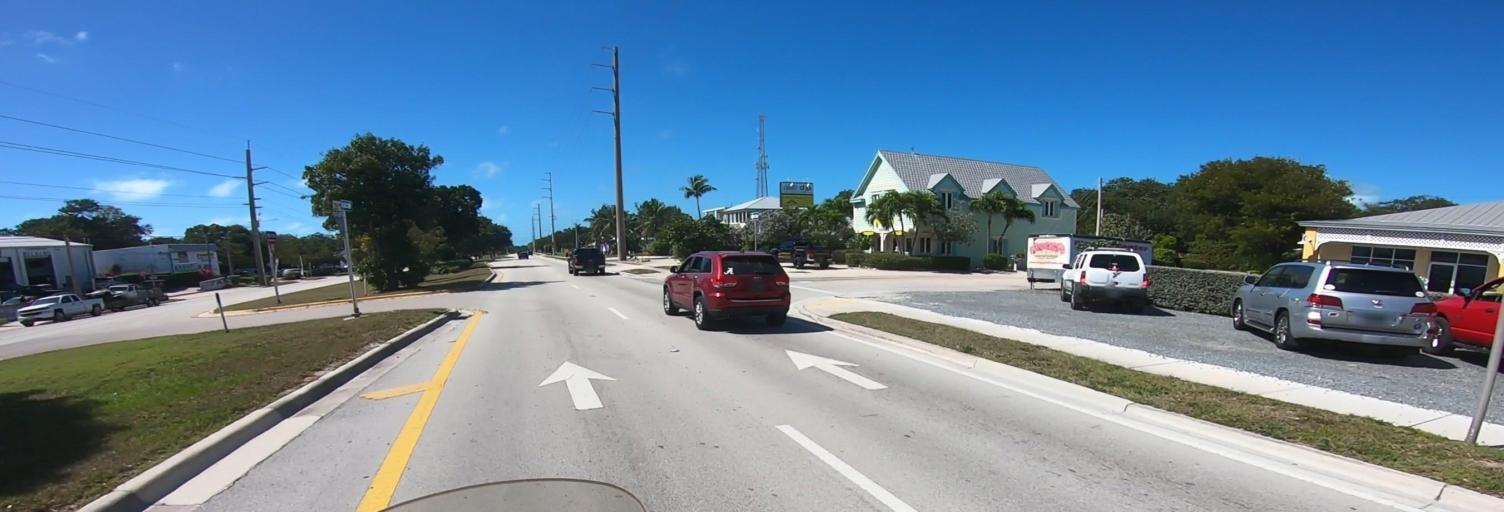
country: US
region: Florida
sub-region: Monroe County
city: Tavernier
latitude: 25.0085
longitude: -80.5173
